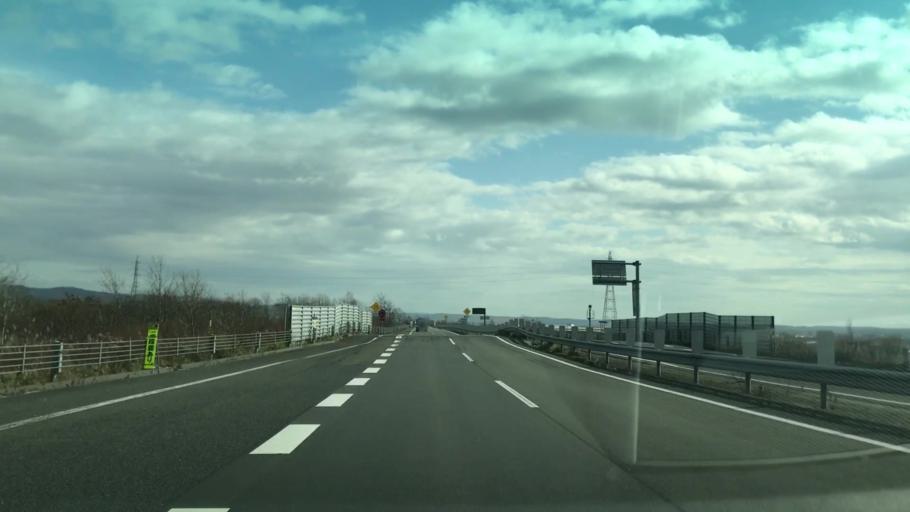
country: JP
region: Hokkaido
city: Tomakomai
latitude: 42.5875
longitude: 141.9330
